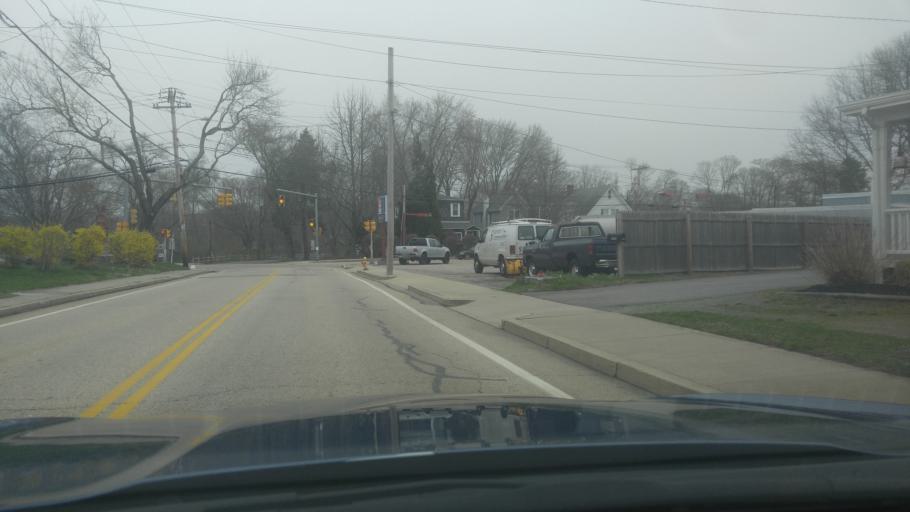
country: US
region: Rhode Island
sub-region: Washington County
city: Narragansett Pier
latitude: 41.4329
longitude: -71.4662
